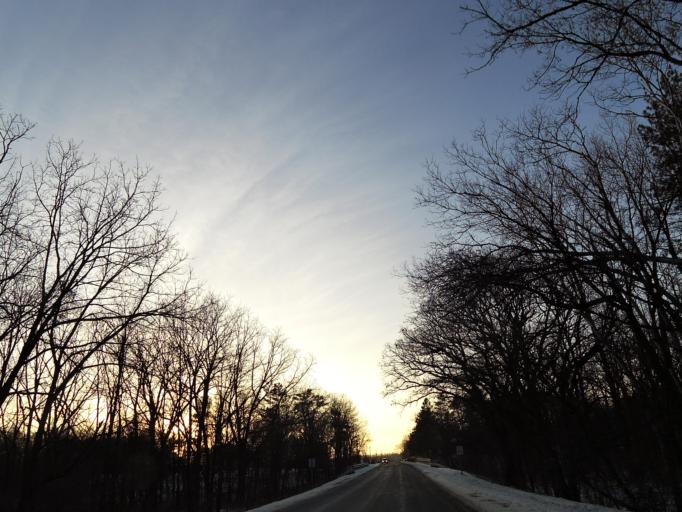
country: US
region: Wisconsin
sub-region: Pierce County
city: River Falls
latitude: 44.8700
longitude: -92.6270
